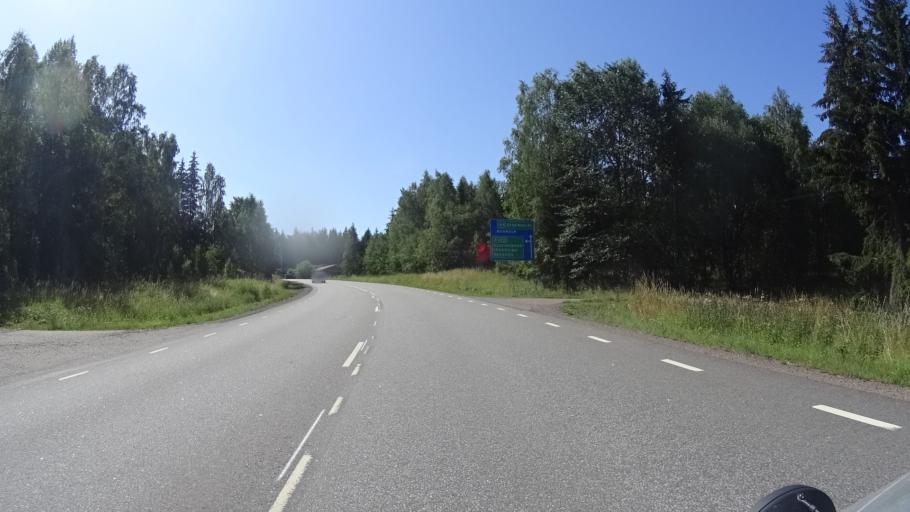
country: SE
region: OEstergoetland
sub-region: Vadstena Kommun
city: Herrestad
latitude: 58.3000
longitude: 14.9199
